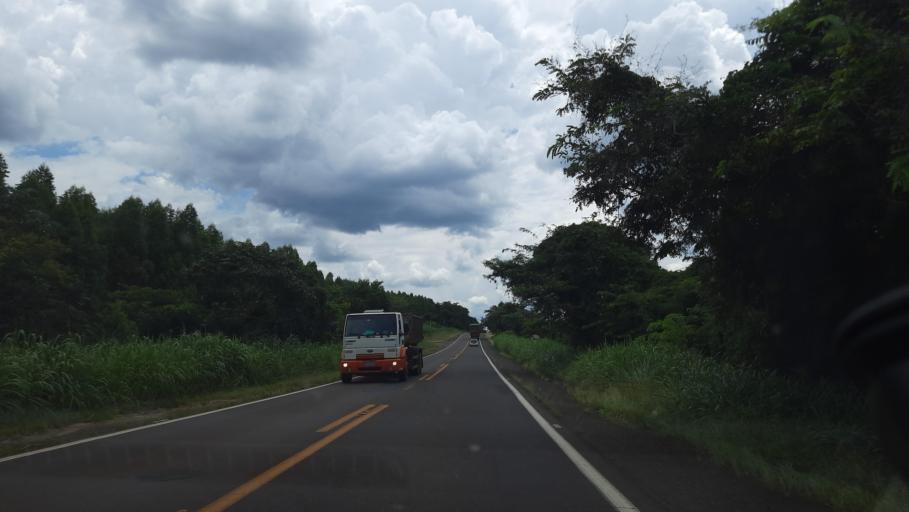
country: BR
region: Sao Paulo
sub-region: Mococa
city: Mococa
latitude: -21.4576
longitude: -47.1192
